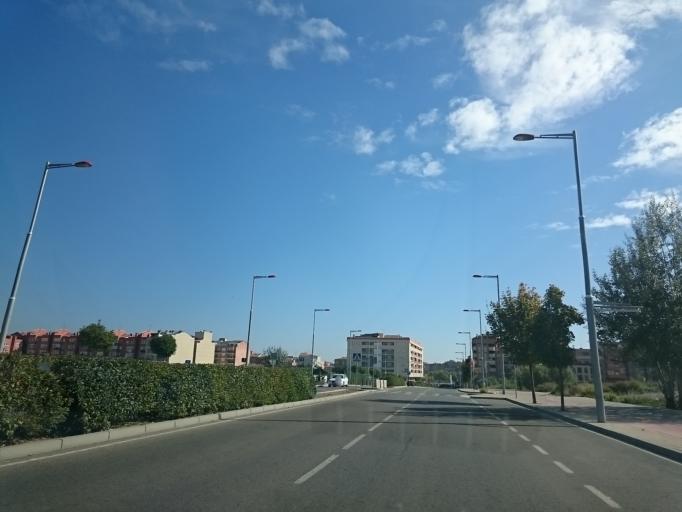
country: ES
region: Catalonia
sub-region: Provincia de Lleida
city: Lleida
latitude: 41.6292
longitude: 0.6183
